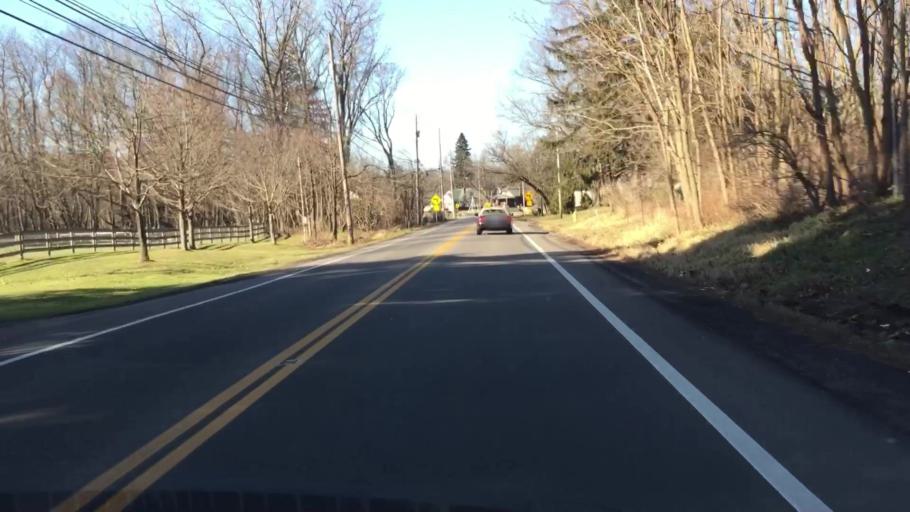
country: US
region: Ohio
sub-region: Summit County
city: Fairlawn
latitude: 41.0874
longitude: -81.6017
